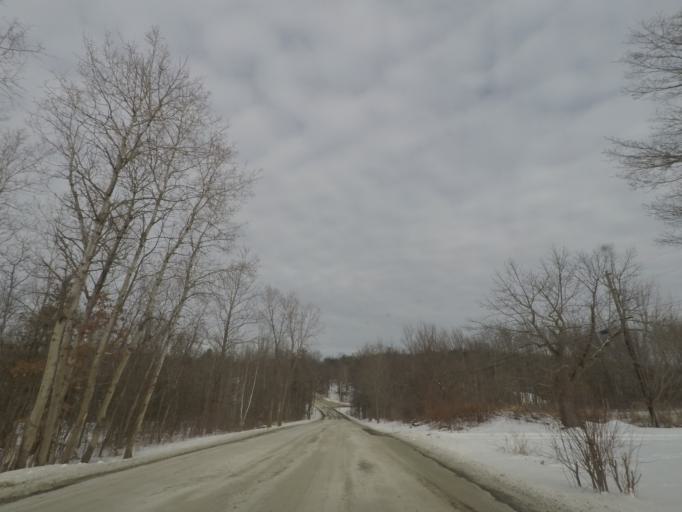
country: US
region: New York
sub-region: Rensselaer County
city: Averill Park
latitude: 42.6145
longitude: -73.5421
